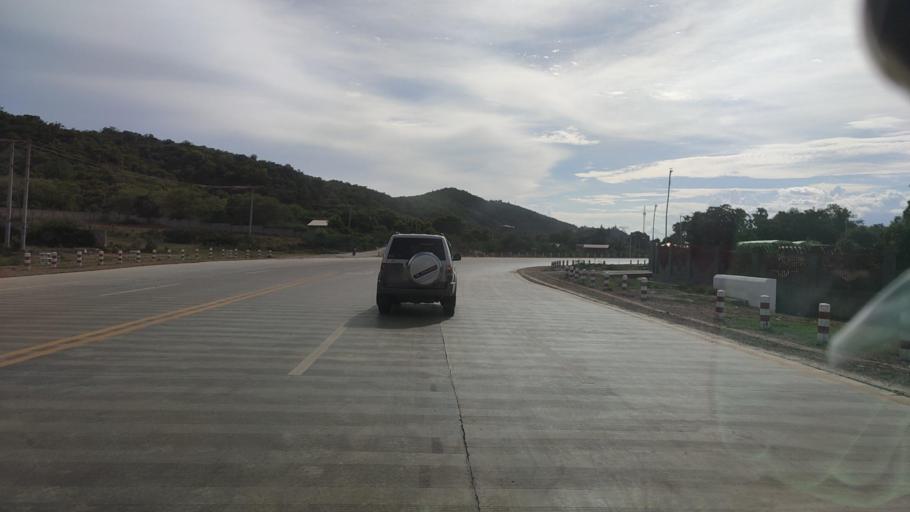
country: MM
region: Mandalay
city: Kyaukse
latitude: 21.6089
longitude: 96.1712
